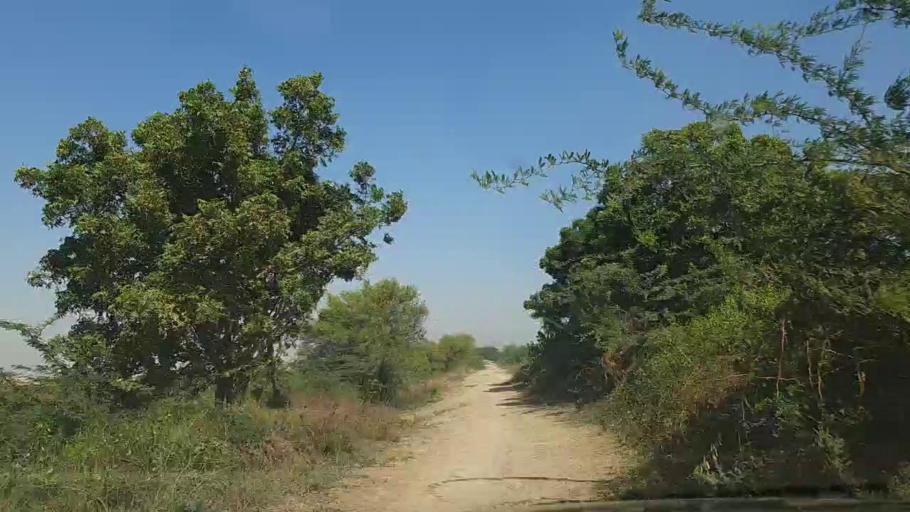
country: PK
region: Sindh
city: Thatta
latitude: 24.8063
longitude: 67.9840
